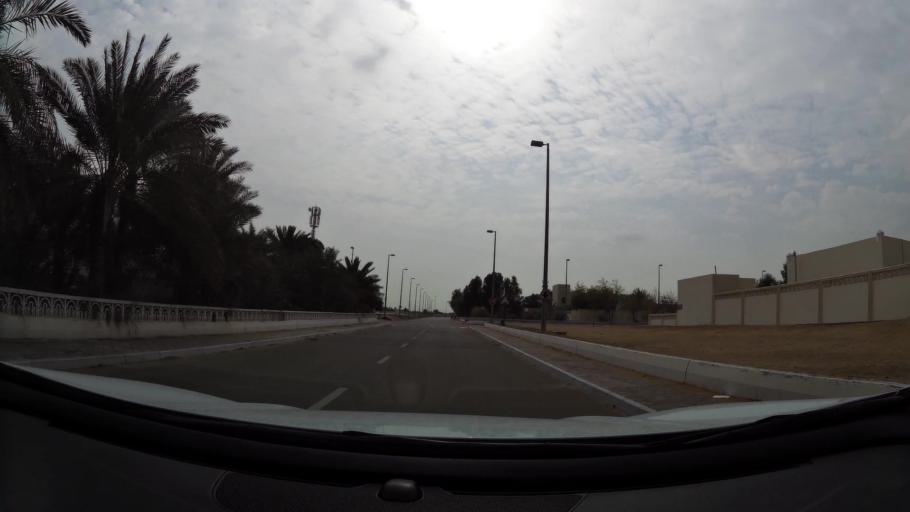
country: AE
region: Abu Dhabi
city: Abu Dhabi
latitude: 24.6473
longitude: 54.7320
